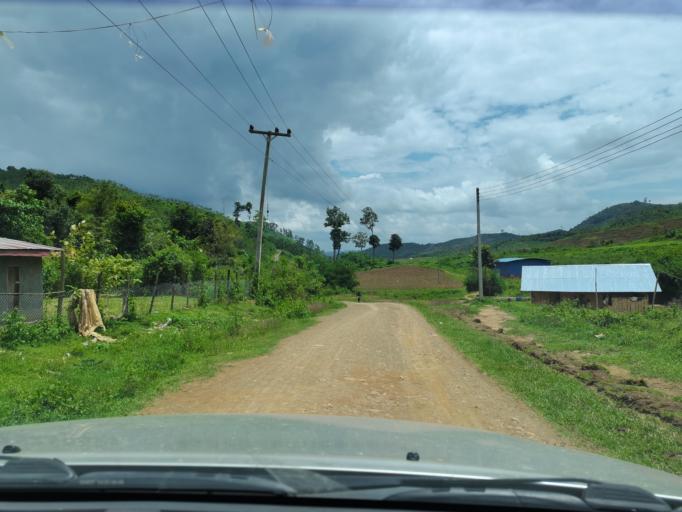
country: LA
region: Loungnamtha
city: Muang Long
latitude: 20.7233
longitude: 101.0142
